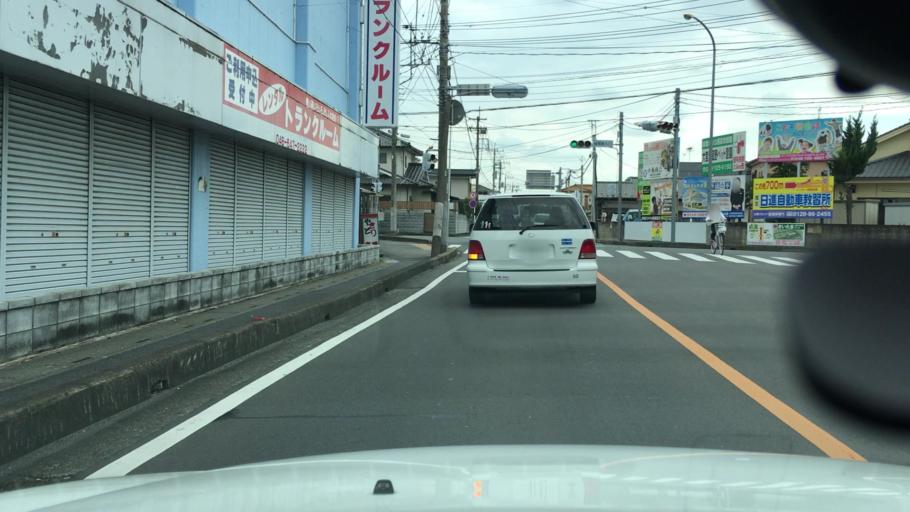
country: JP
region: Saitama
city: Kamifukuoka
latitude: 35.9149
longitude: 139.5655
